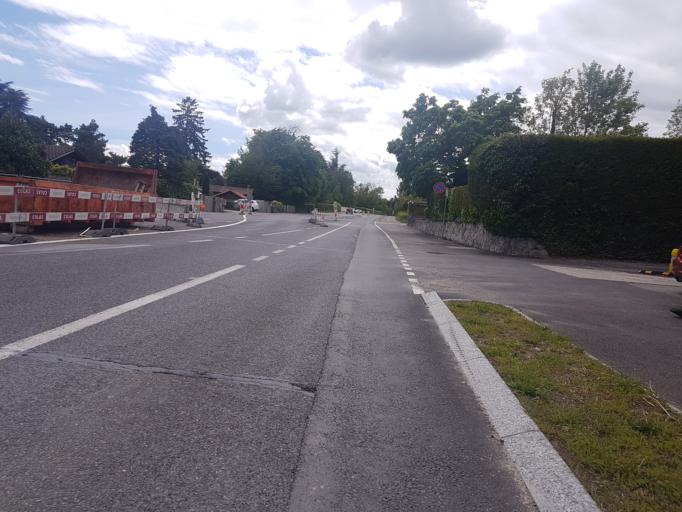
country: CH
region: Vaud
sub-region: Nyon District
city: Coppet
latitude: 46.3047
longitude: 6.1801
